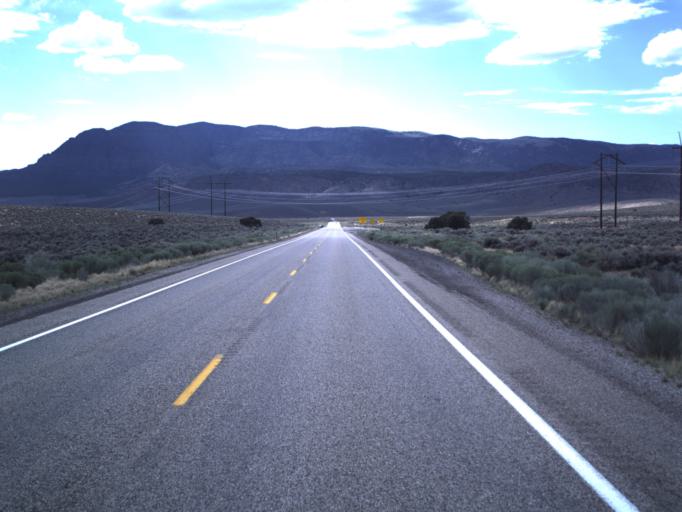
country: US
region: Utah
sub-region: Beaver County
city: Beaver
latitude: 38.0600
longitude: -112.6572
